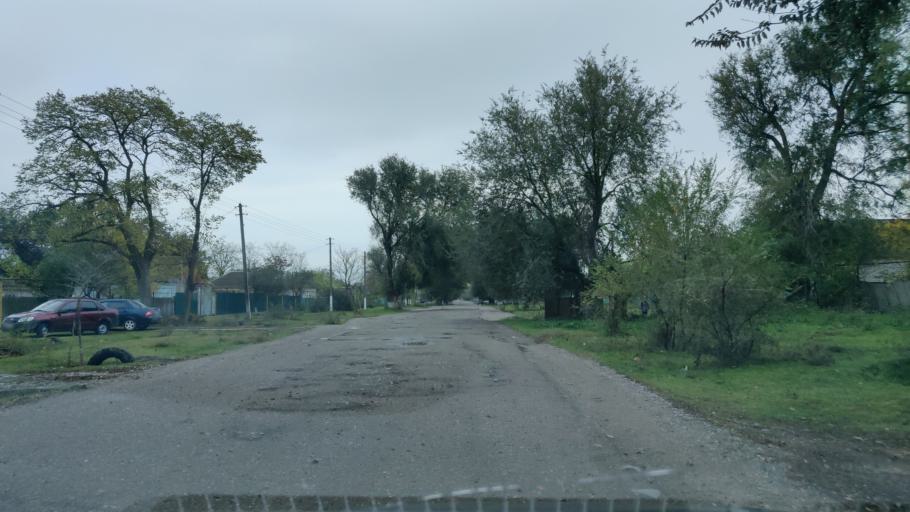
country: RU
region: Stavropol'skiy
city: Irgakly
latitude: 44.2420
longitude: 44.7216
